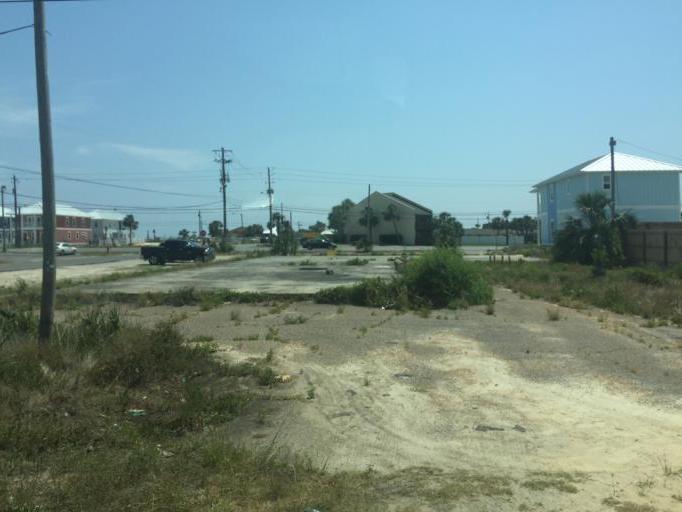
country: US
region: Florida
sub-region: Bay County
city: Lower Grand Lagoon
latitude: 30.1457
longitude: -85.7571
